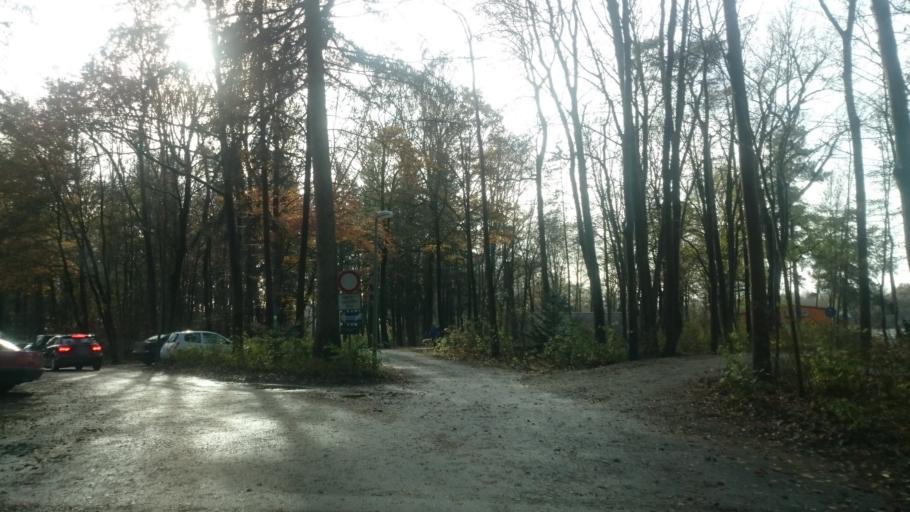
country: DE
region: Bavaria
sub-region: Swabia
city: Friedberg
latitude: 48.3445
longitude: 10.9385
